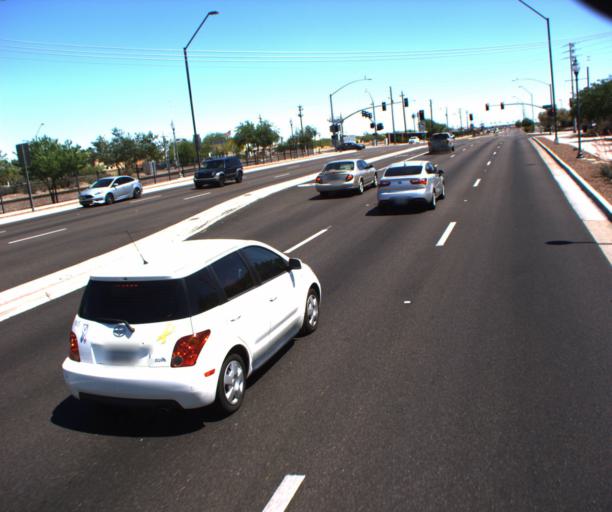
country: US
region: Arizona
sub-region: Maricopa County
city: Peoria
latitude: 33.5816
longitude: -112.2380
